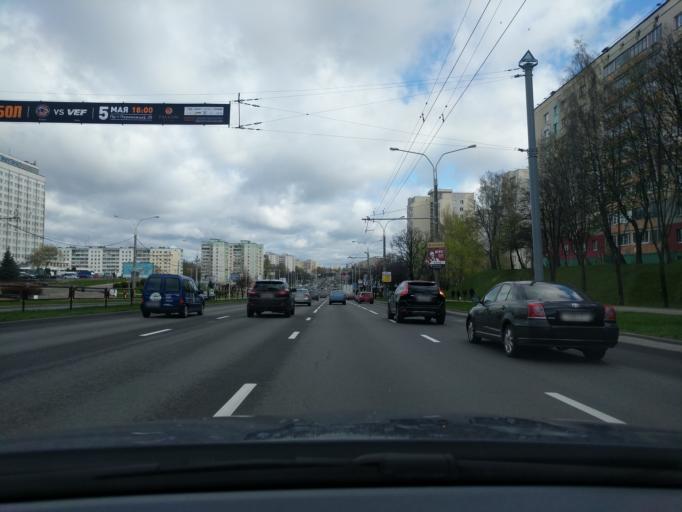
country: BY
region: Minsk
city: Novoye Medvezhino
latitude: 53.9066
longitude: 27.4961
